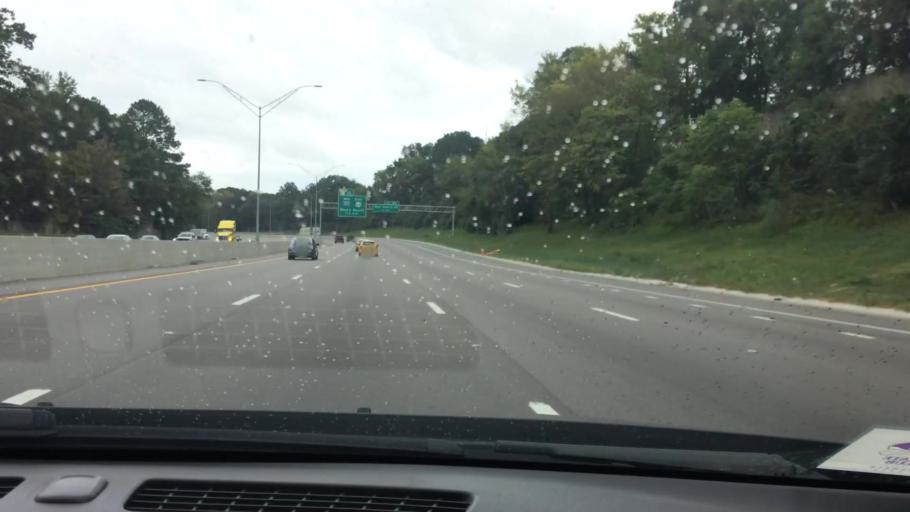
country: US
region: North Carolina
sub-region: Wake County
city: Raleigh
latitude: 35.7527
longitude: -78.6269
